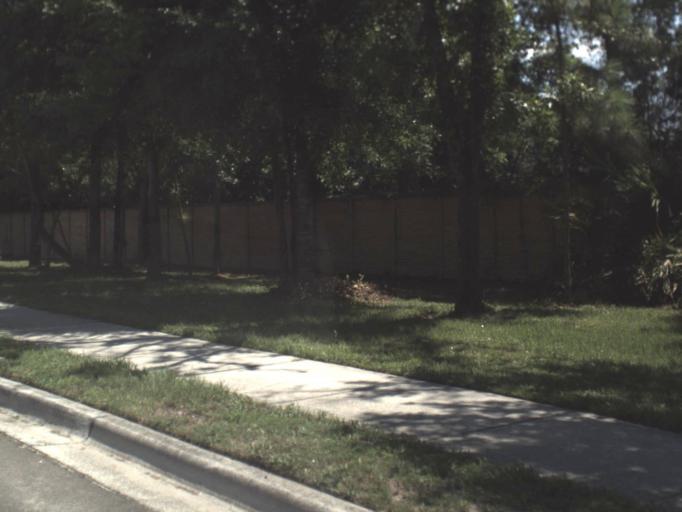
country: US
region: Florida
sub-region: Saint Johns County
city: Fruit Cove
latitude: 30.0926
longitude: -81.6281
